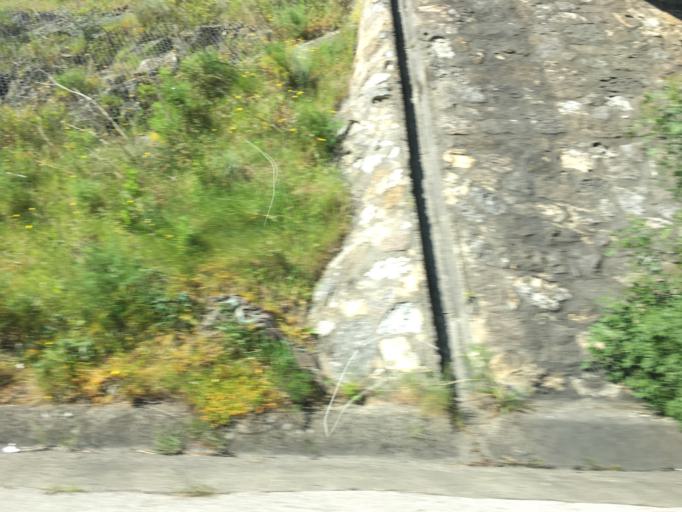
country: PT
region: Lisbon
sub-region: Odivelas
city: Famoes
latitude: 38.7844
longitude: -9.2309
